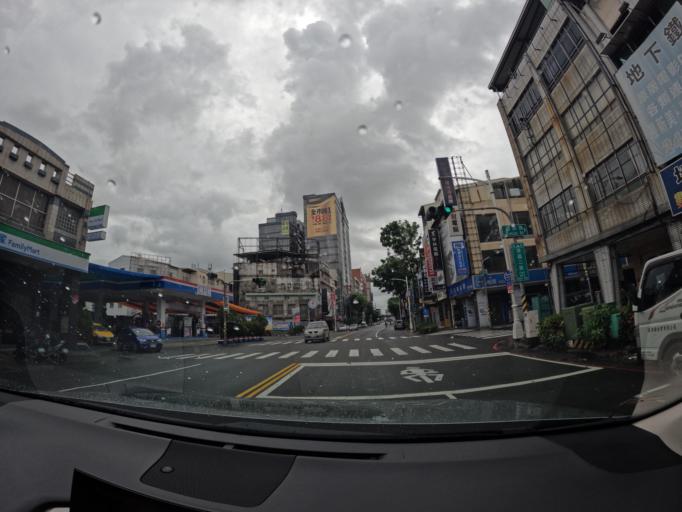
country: TW
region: Kaohsiung
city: Kaohsiung
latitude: 22.6375
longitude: 120.3106
